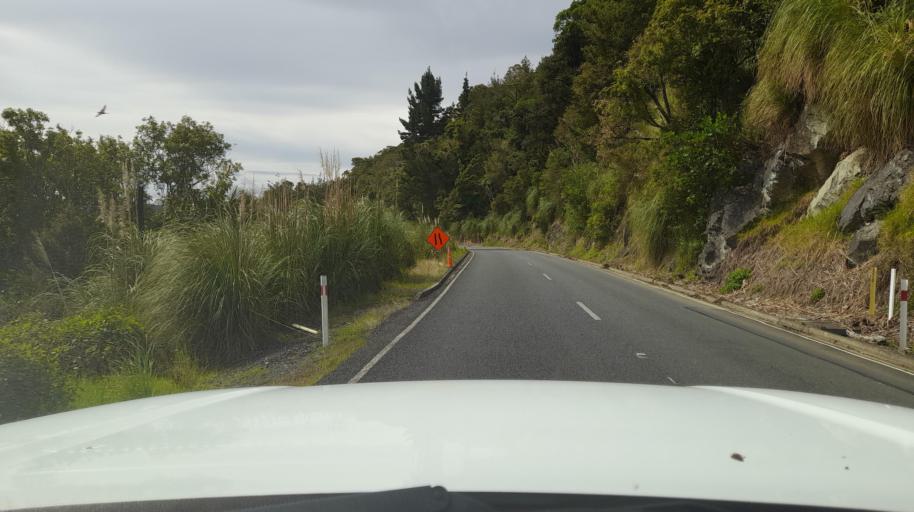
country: NZ
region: Northland
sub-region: Far North District
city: Taipa
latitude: -35.2523
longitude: 173.5327
